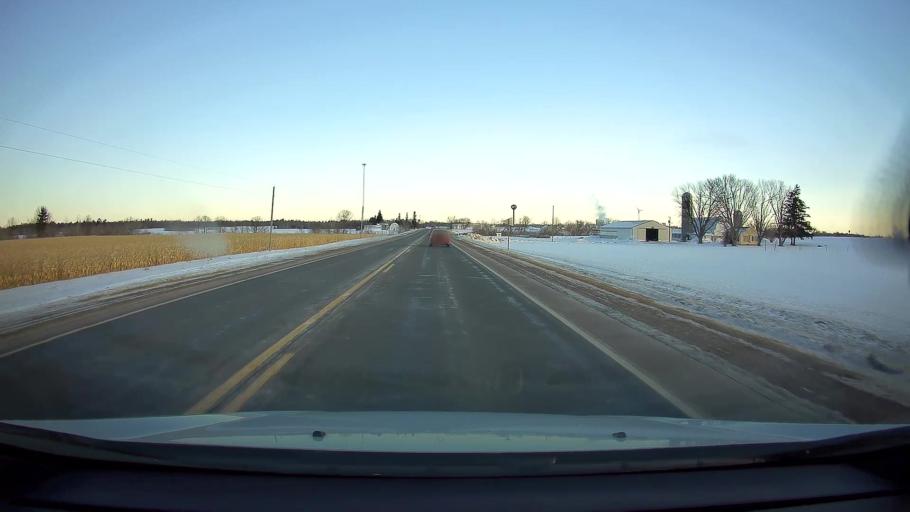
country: US
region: Wisconsin
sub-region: Barron County
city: Turtle Lake
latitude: 45.3820
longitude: -92.1667
